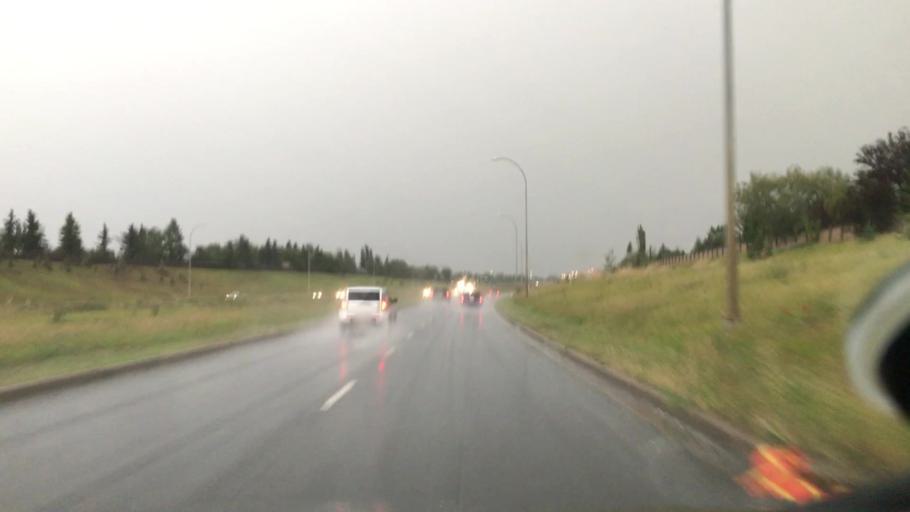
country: CA
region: Alberta
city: Edmonton
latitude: 53.4703
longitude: -113.5795
